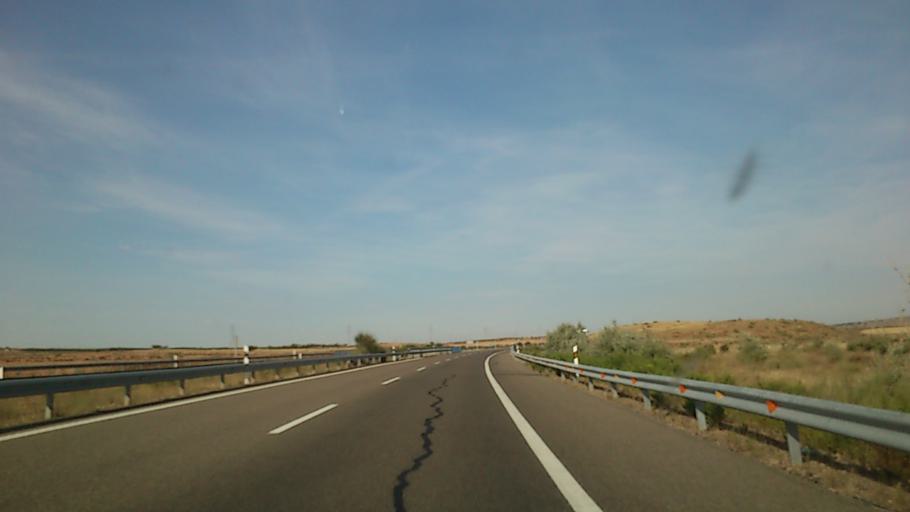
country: ES
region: Aragon
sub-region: Provincia de Zaragoza
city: Longares
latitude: 41.4072
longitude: -1.1756
